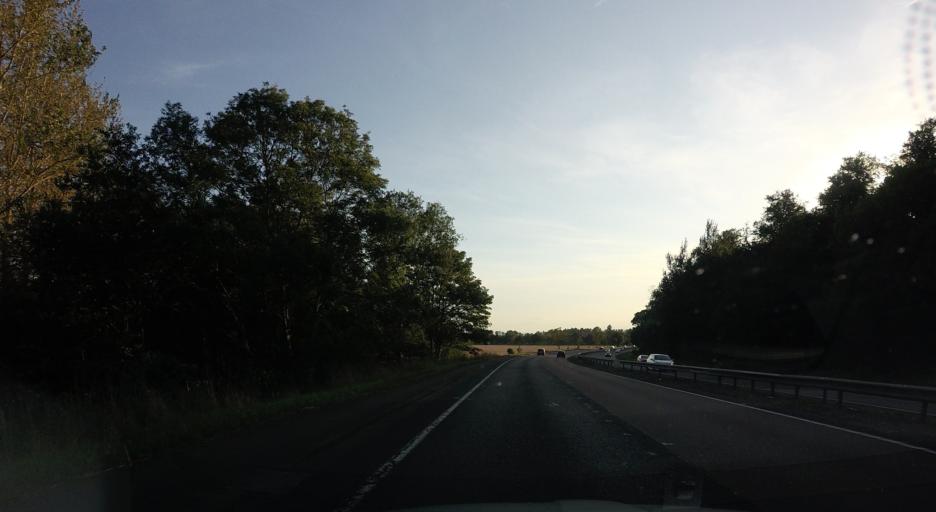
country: GB
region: Scotland
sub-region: Perth and Kinross
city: Errol
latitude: 56.4543
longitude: -3.1486
